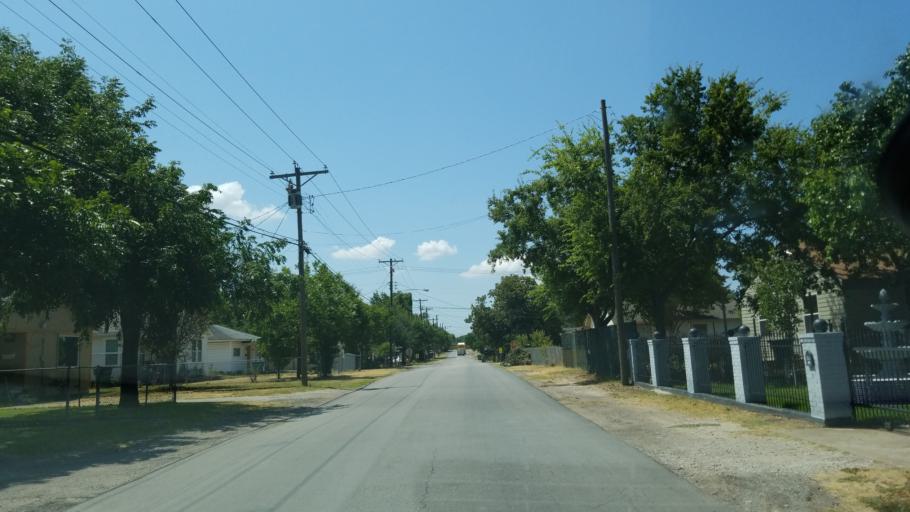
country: US
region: Texas
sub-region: Dallas County
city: Cockrell Hill
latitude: 32.7418
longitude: -96.8927
